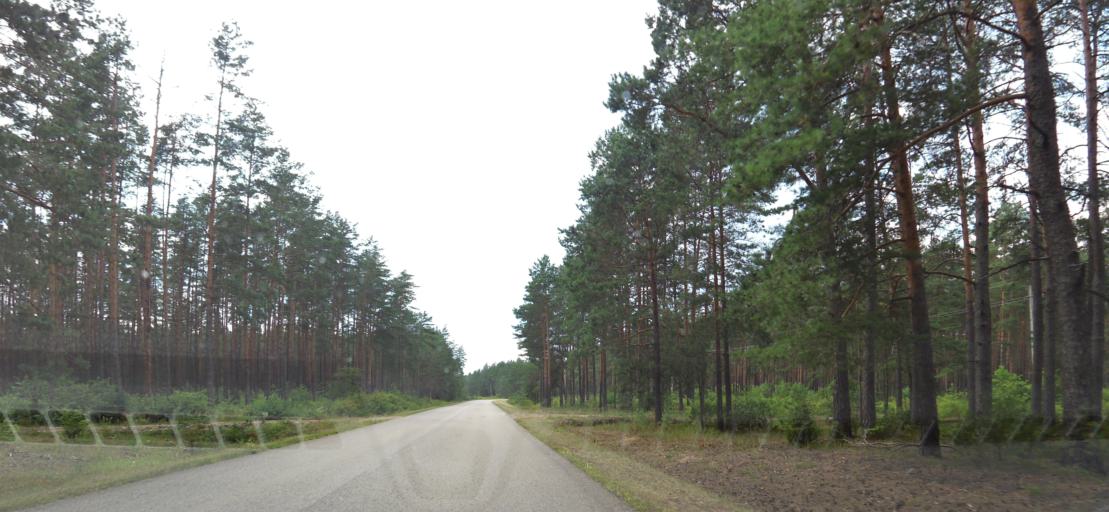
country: LT
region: Alytaus apskritis
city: Druskininkai
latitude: 53.9888
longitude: 24.1247
